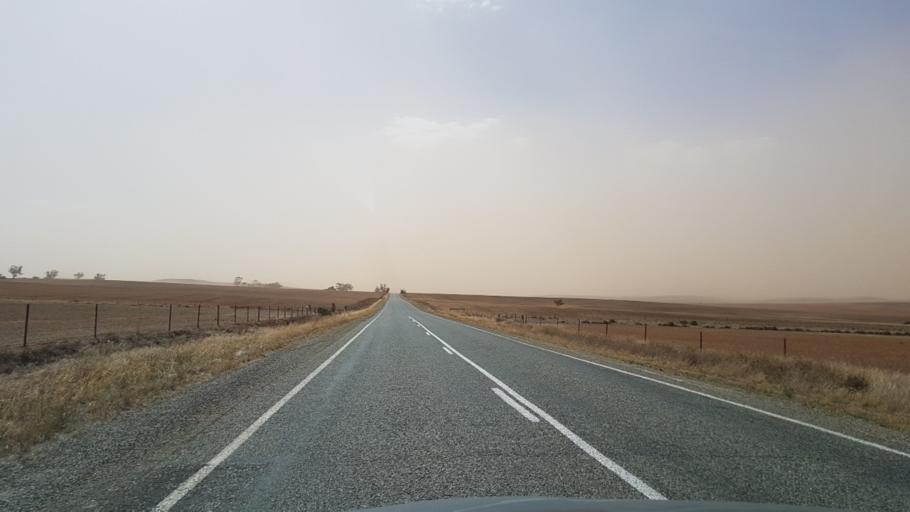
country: AU
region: South Australia
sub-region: Northern Areas
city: Jamestown
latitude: -33.3468
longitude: 138.8915
